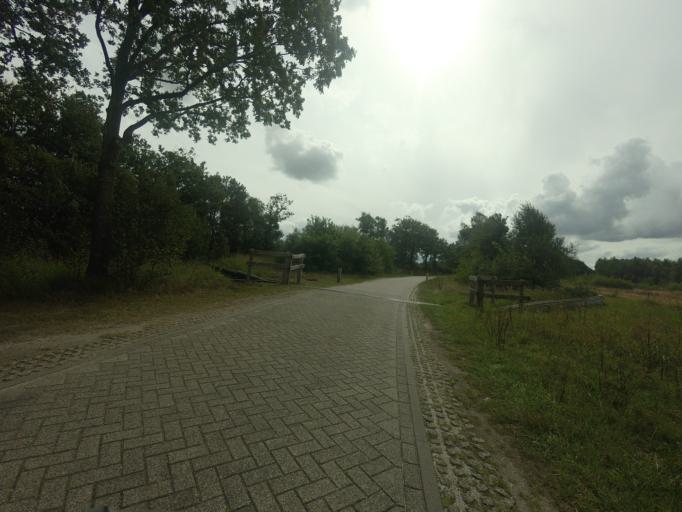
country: NL
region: Drenthe
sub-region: Gemeente Westerveld
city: Dwingeloo
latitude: 52.9939
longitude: 6.3794
